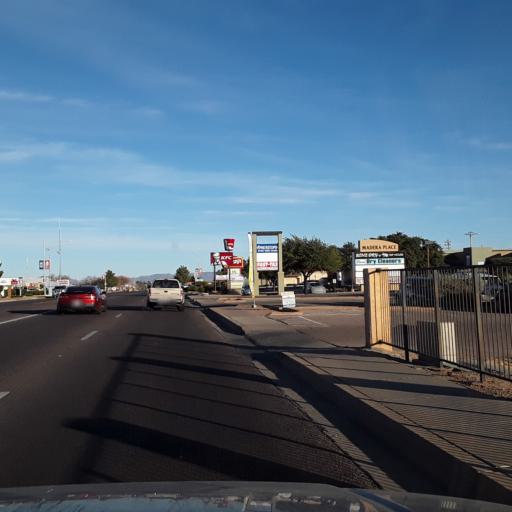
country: US
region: Arizona
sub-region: Cochise County
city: Sierra Vista
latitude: 31.5546
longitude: -110.2892
